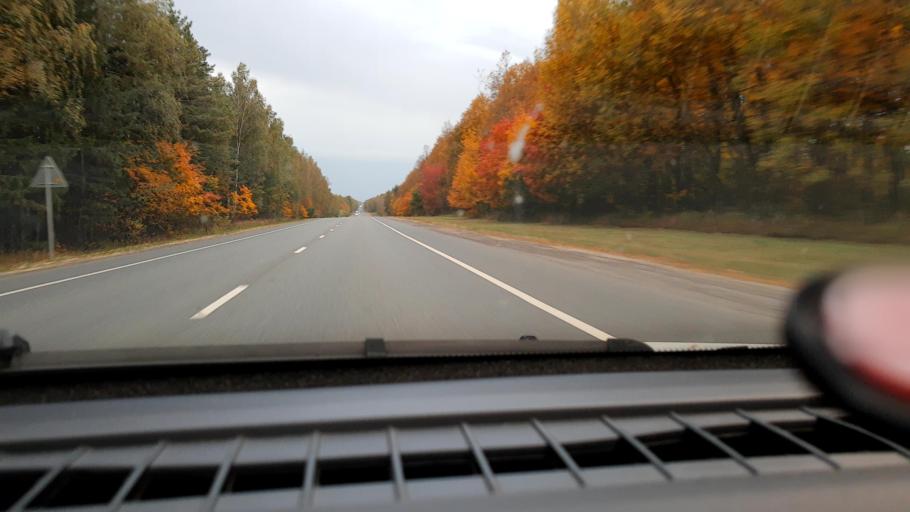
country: RU
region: Vladimir
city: Orgtrud
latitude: 56.2002
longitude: 40.8111
